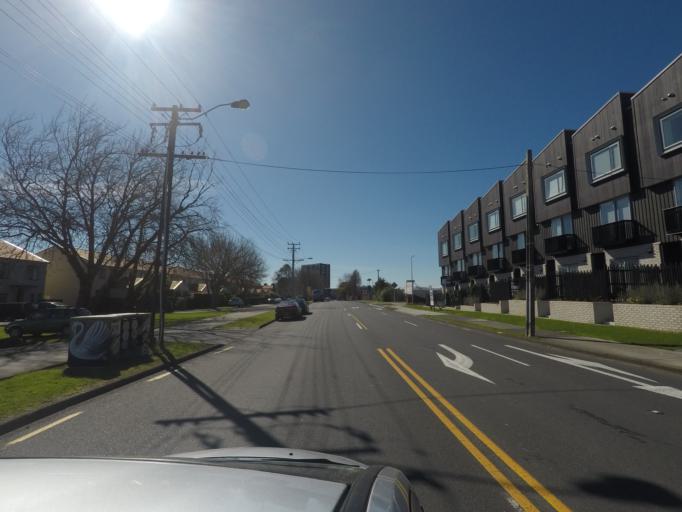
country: NZ
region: Auckland
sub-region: Auckland
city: Waitakere
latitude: -36.9133
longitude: 174.6816
